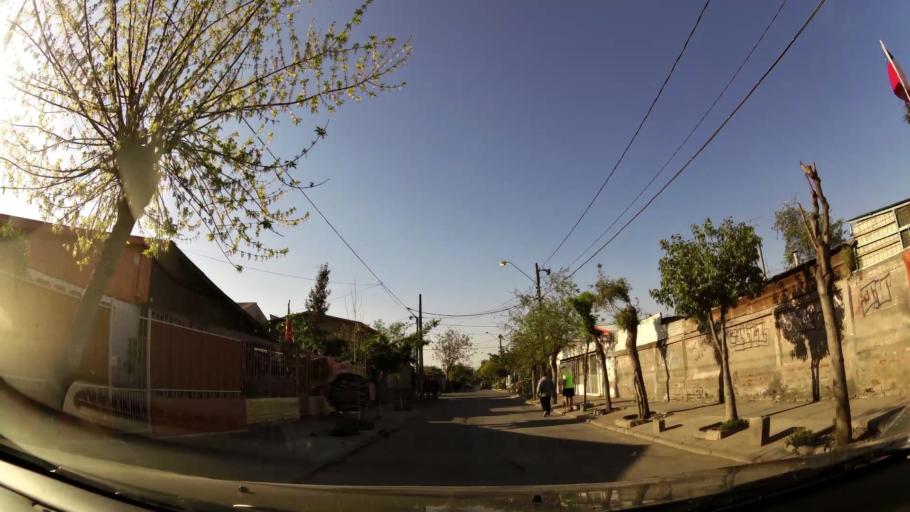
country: CL
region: Santiago Metropolitan
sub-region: Provincia de Santiago
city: La Pintana
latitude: -33.5845
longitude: -70.6619
